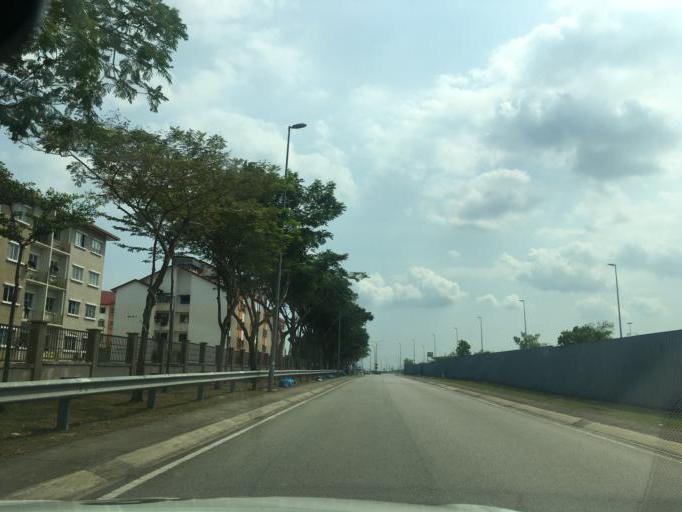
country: MY
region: Selangor
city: Shah Alam
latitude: 3.0818
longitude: 101.4788
